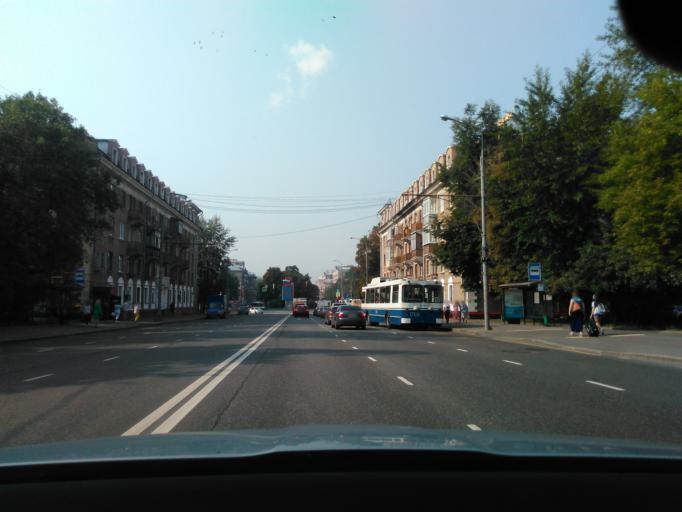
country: RU
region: Moscow
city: Sokol
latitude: 55.8009
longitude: 37.5164
